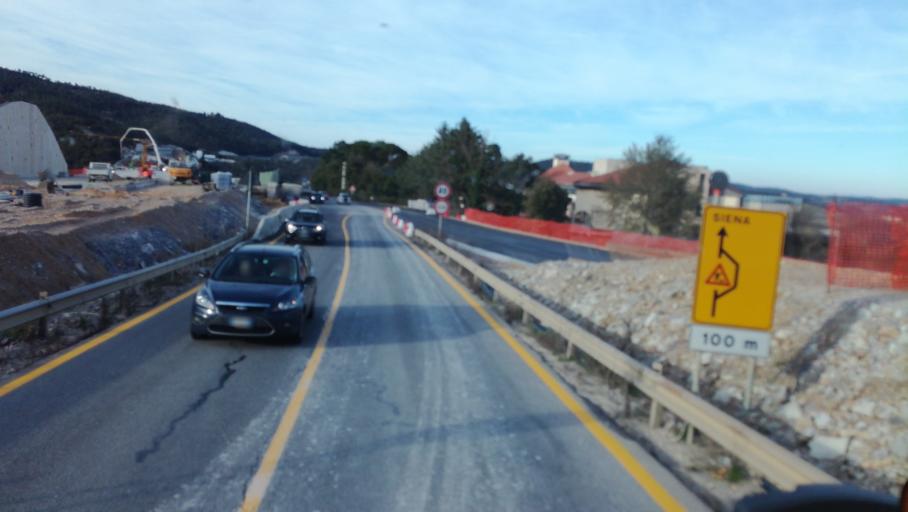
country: IT
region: Tuscany
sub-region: Provincia di Grosseto
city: Civitella Marittima
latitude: 43.0735
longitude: 11.2970
